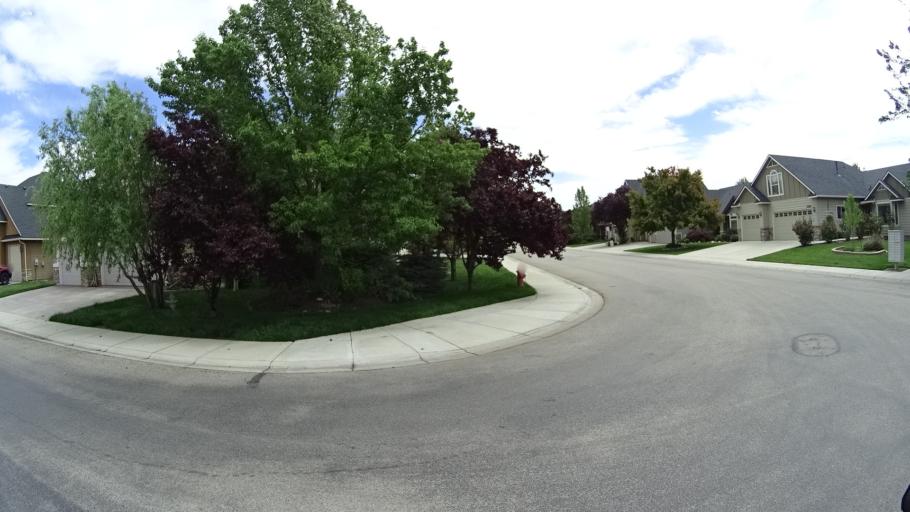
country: US
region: Idaho
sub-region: Ada County
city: Meridian
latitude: 43.6286
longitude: -116.3270
